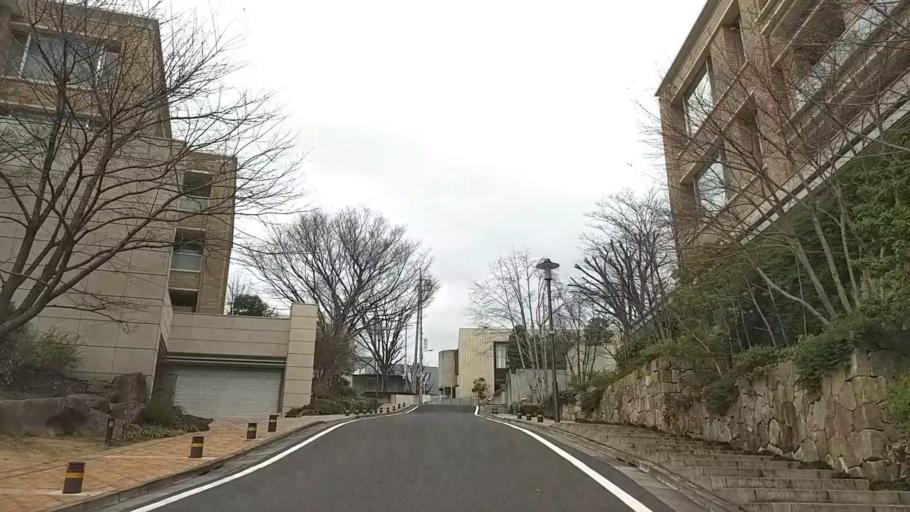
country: JP
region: Tokyo
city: Tokyo
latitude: 35.6247
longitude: 139.7330
